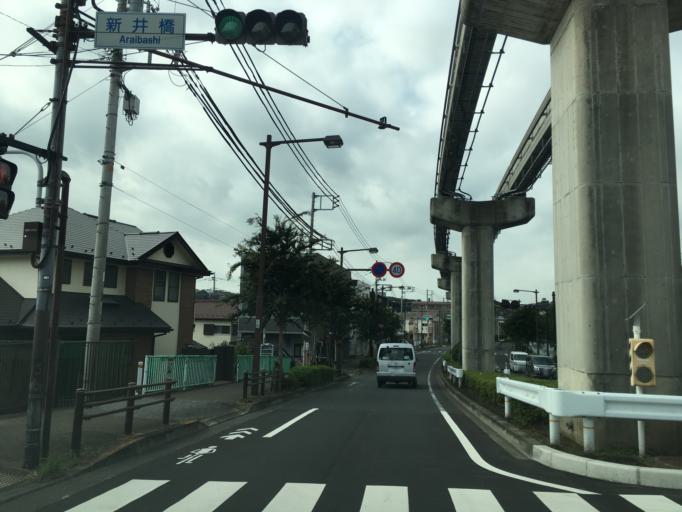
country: JP
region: Tokyo
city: Hino
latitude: 35.6662
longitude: 139.4193
